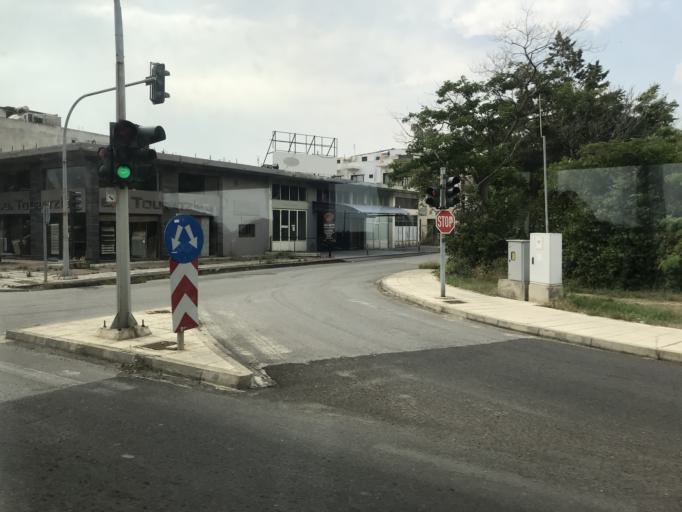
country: GR
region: East Macedonia and Thrace
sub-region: Nomos Evrou
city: Alexandroupoli
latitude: 40.8491
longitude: 25.8946
